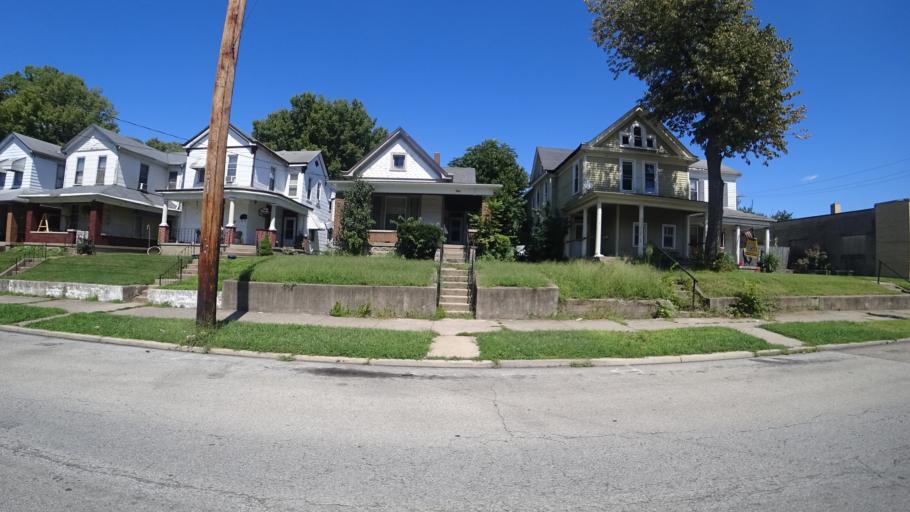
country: US
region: Ohio
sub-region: Butler County
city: Hamilton
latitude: 39.4011
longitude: -84.5483
